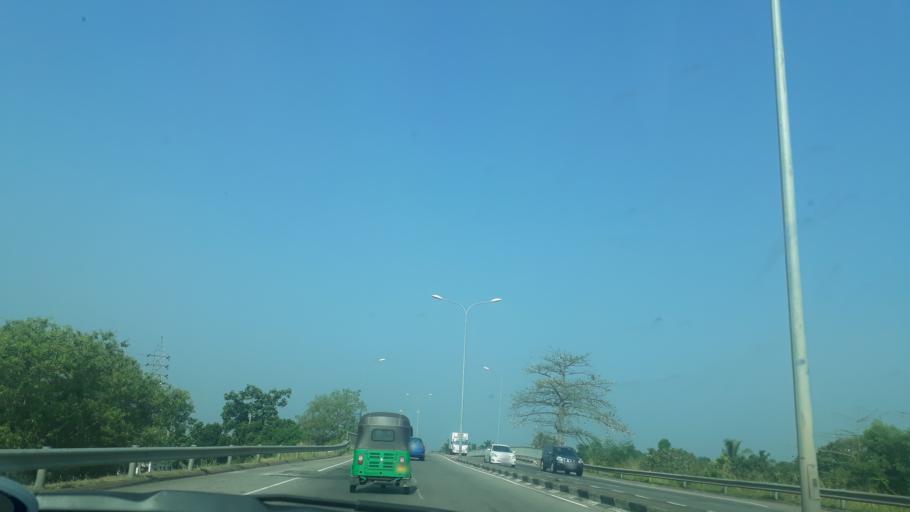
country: LK
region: Western
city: Wattala
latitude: 6.9688
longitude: 79.8991
